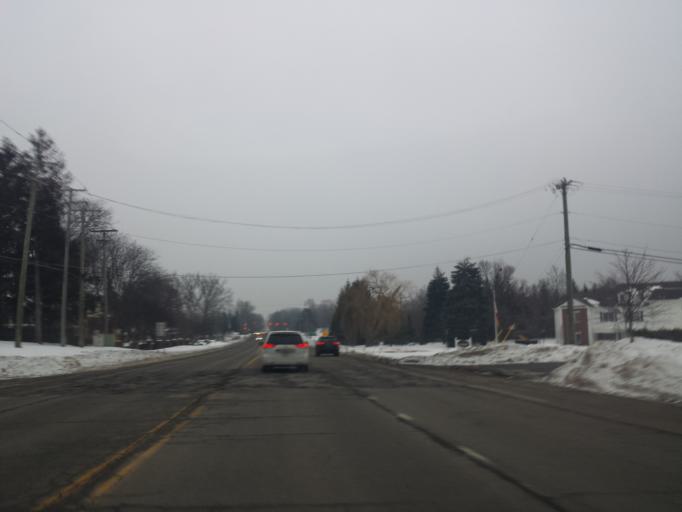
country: US
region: Michigan
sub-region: Oakland County
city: Franklin
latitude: 42.5173
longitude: -83.3401
